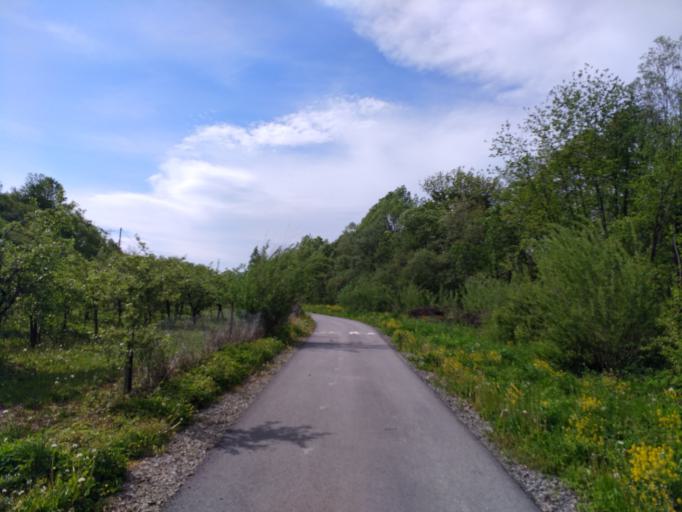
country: PL
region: Lesser Poland Voivodeship
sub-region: Powiat nowosadecki
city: Lacko
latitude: 49.5705
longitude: 20.4271
